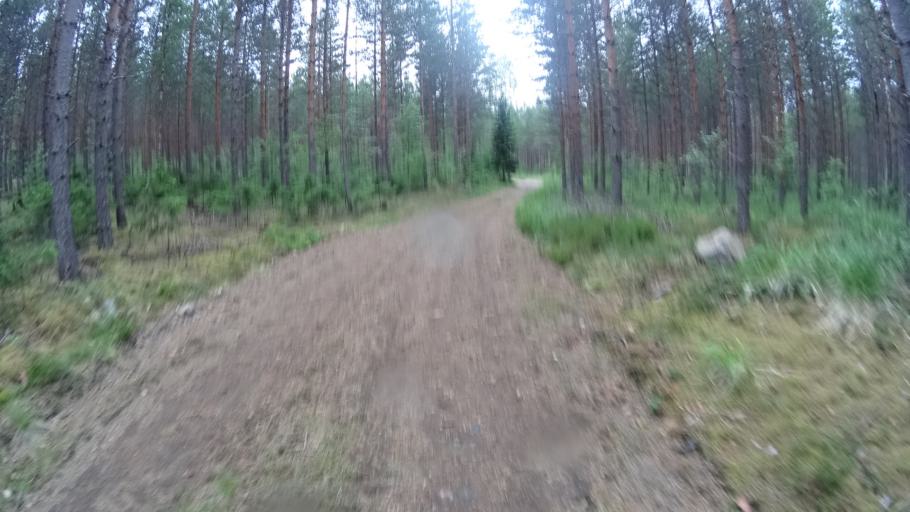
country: FI
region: Uusimaa
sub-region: Helsinki
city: Karkkila
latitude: 60.5946
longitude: 24.1786
